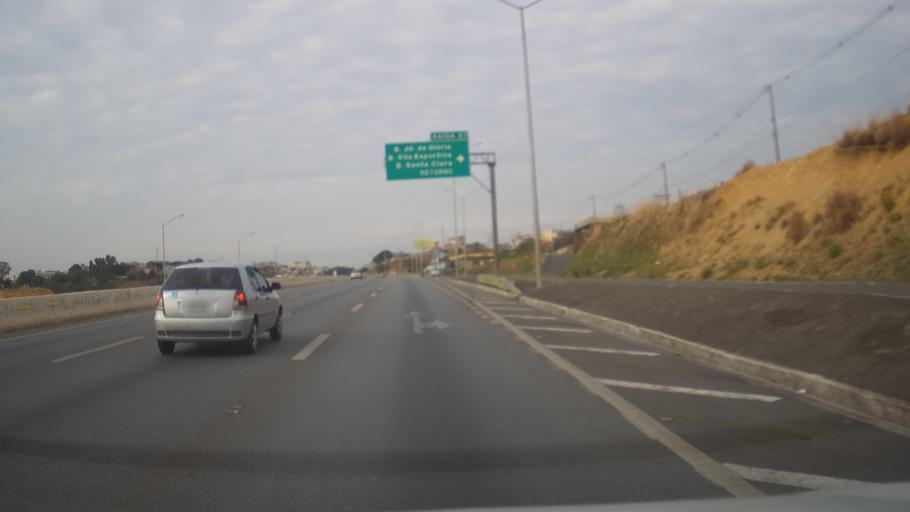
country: BR
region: Minas Gerais
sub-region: Vespasiano
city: Vespasiano
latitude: -19.7408
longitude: -43.9493
